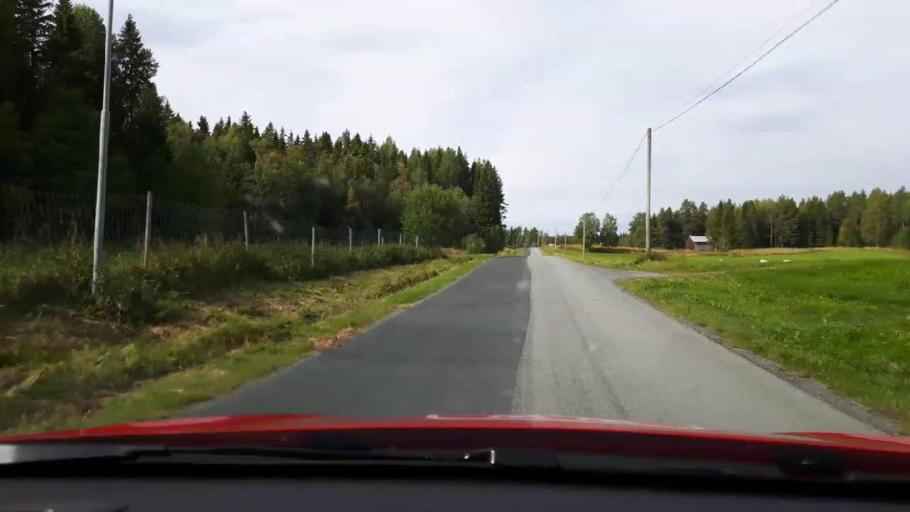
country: SE
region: Jaemtland
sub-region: Krokoms Kommun
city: Valla
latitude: 63.2734
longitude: 13.8897
